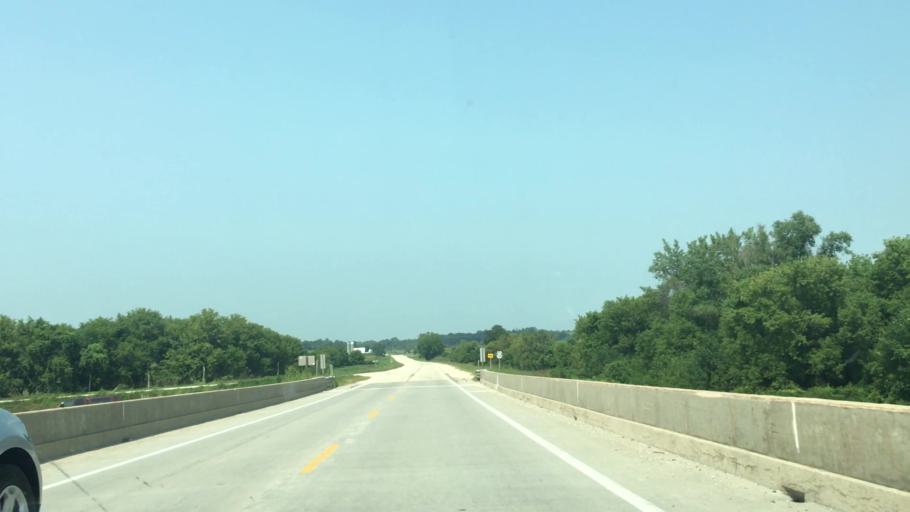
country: US
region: Iowa
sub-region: Fayette County
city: West Union
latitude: 43.0512
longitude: -91.8395
